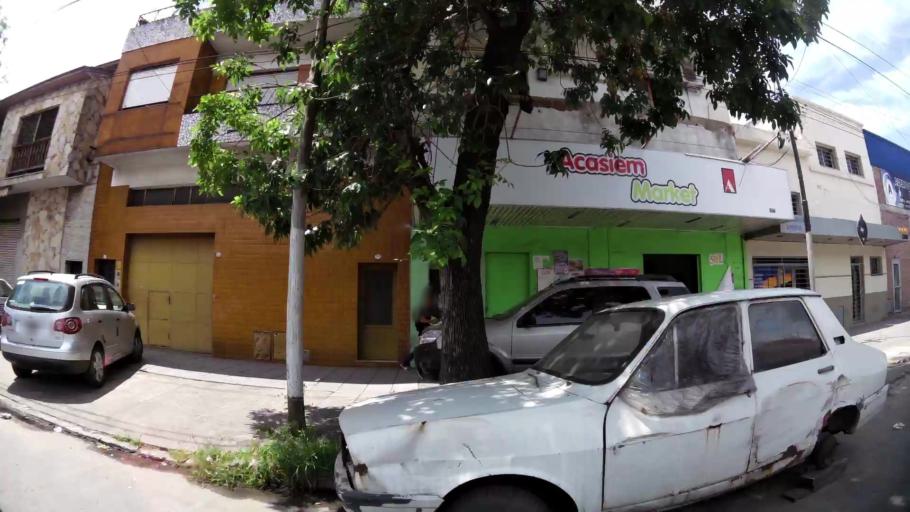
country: AR
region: Buenos Aires
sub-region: Partido de Lanus
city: Lanus
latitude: -34.6764
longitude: -58.4082
